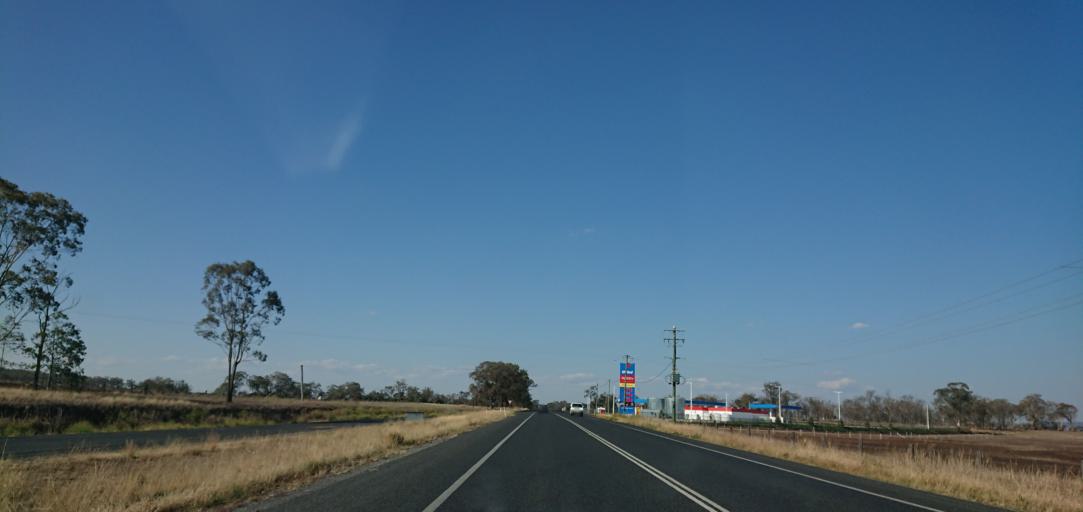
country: AU
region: Queensland
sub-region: Toowoomba
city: Westbrook
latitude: -27.6380
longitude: 151.7415
